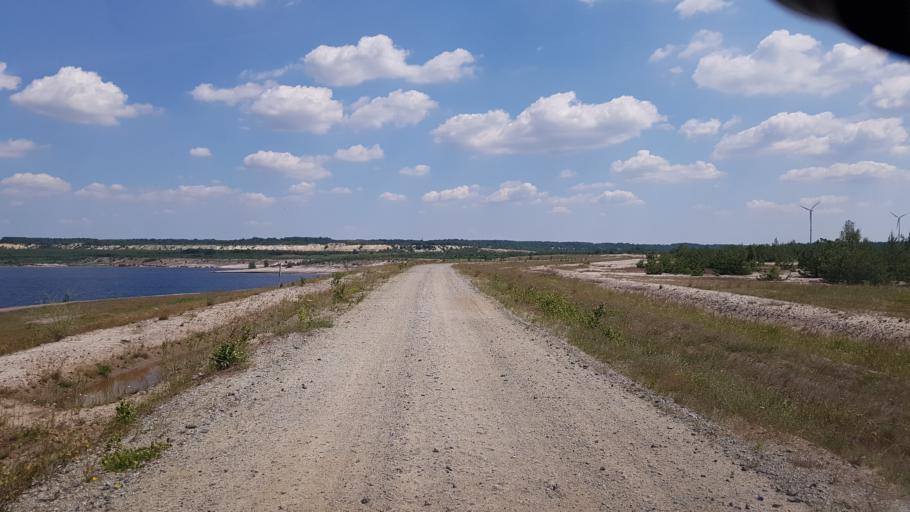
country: DE
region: Brandenburg
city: Sallgast
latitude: 51.5585
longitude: 13.7912
